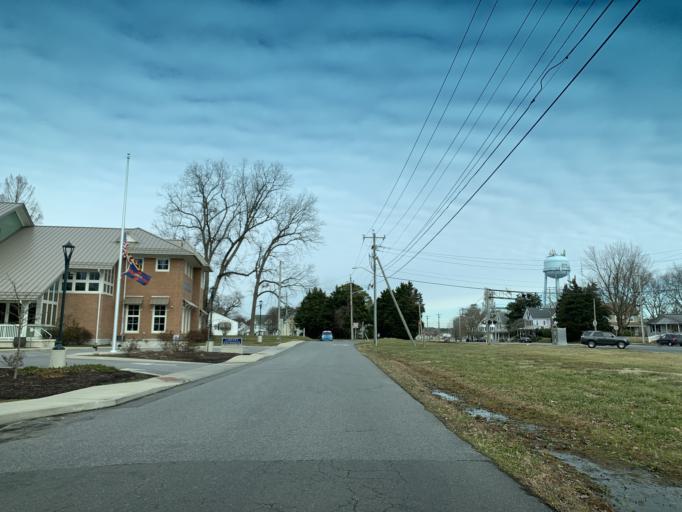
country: US
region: Maryland
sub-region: Worcester County
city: Berlin
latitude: 38.3299
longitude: -75.2211
